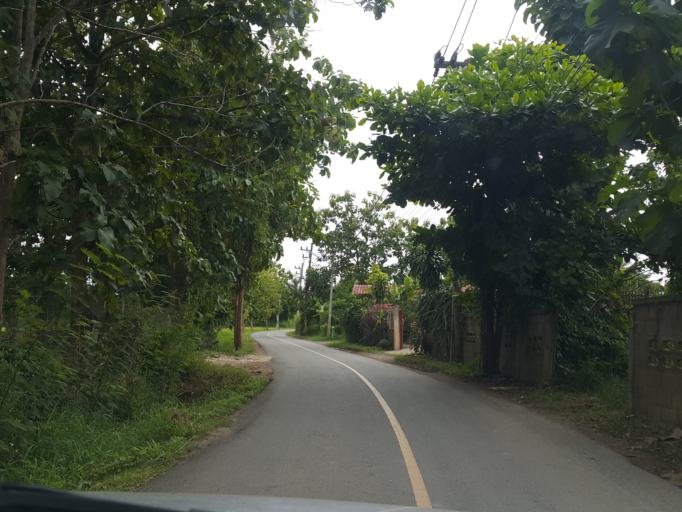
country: TH
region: Chiang Mai
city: San Sai
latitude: 18.8432
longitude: 99.1405
